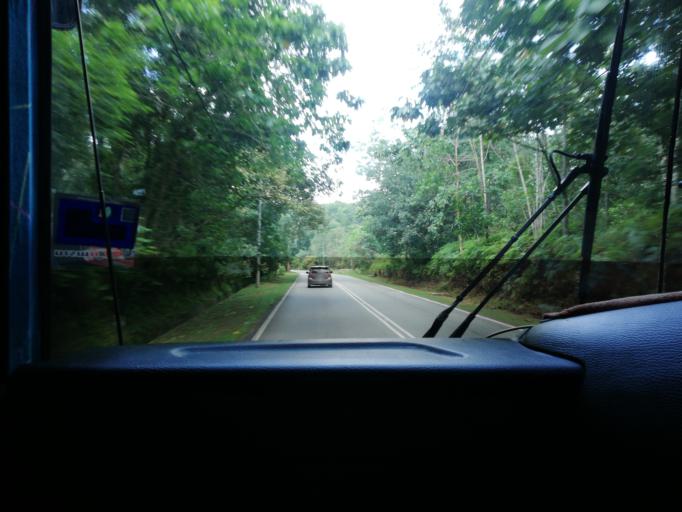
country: MY
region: Kedah
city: Kulim
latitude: 5.2796
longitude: 100.6206
